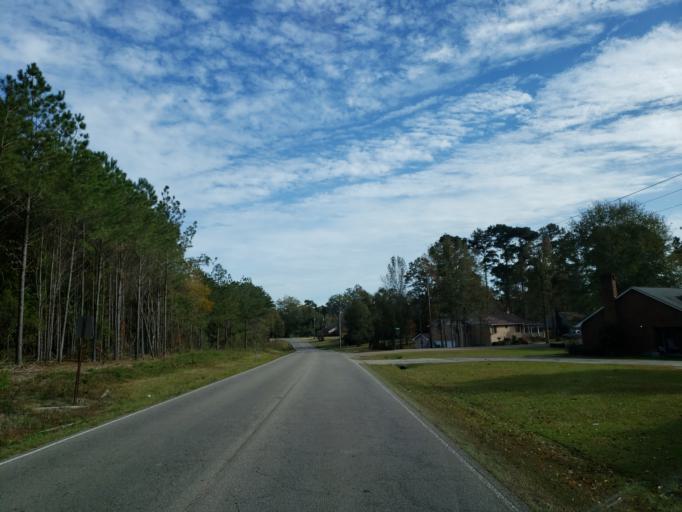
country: US
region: Mississippi
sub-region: Lamar County
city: West Hattiesburg
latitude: 31.3054
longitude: -89.3859
